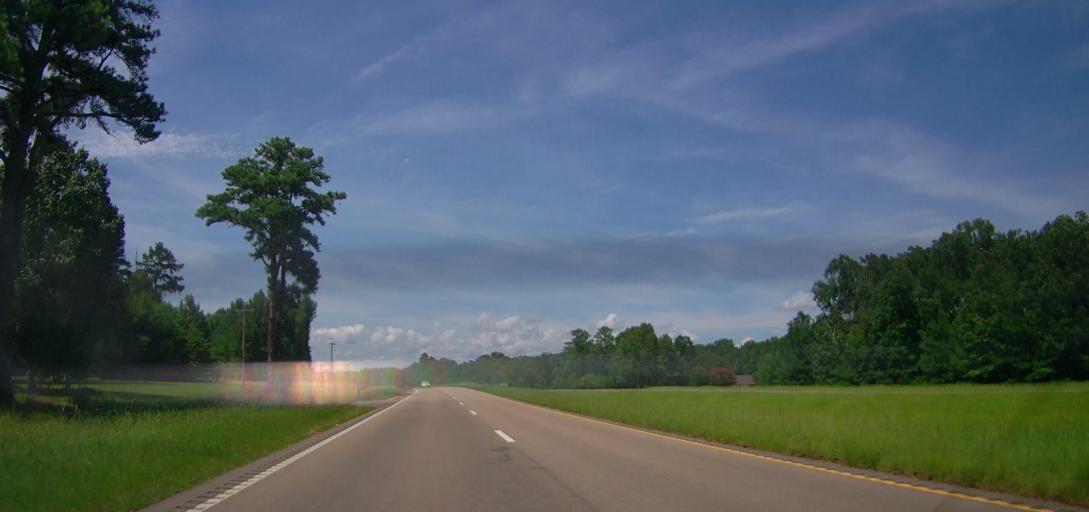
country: US
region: Mississippi
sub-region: Monroe County
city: Amory
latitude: 33.9371
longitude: -88.5974
